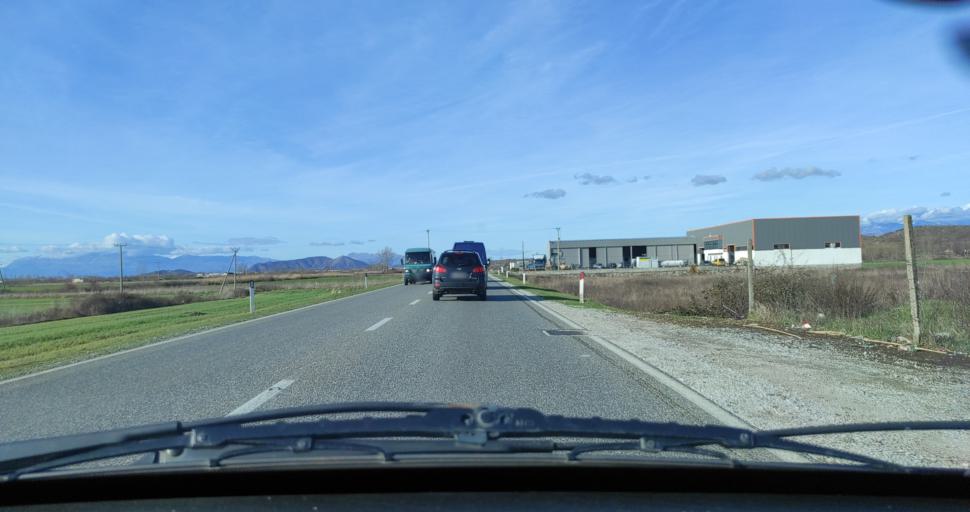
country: AL
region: Lezhe
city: Shengjin
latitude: 41.8571
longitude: 19.5678
